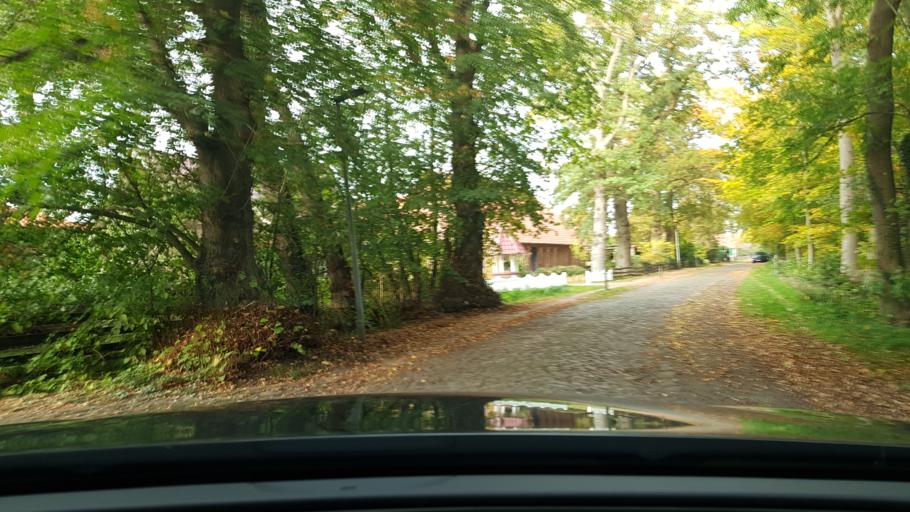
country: DE
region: Lower Saxony
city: Beverstedt
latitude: 53.4235
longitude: 8.8118
